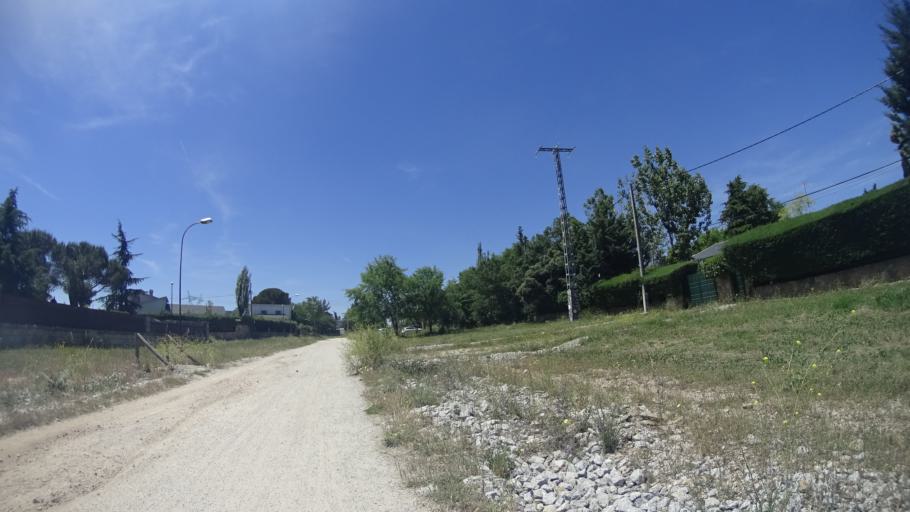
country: ES
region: Madrid
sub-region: Provincia de Madrid
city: Navalquejigo
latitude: 40.6216
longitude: -4.0314
